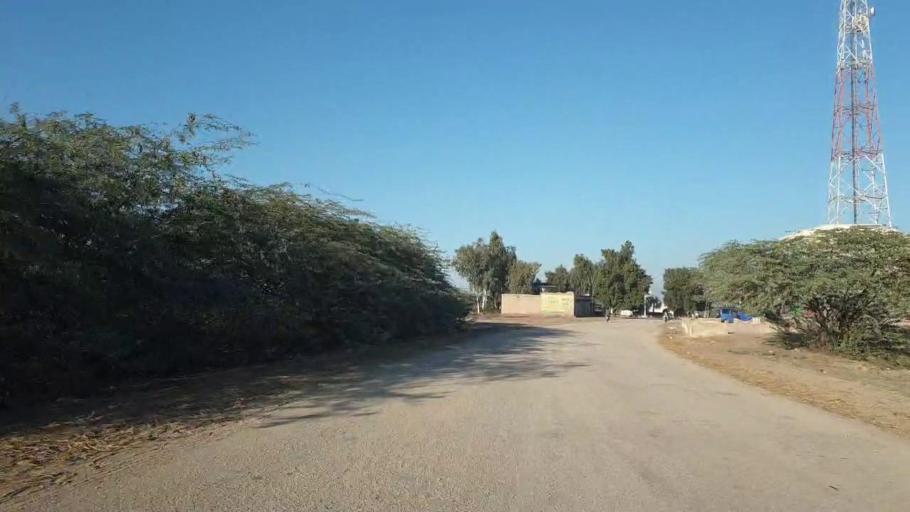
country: PK
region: Sindh
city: Dokri
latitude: 27.3676
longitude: 68.1162
